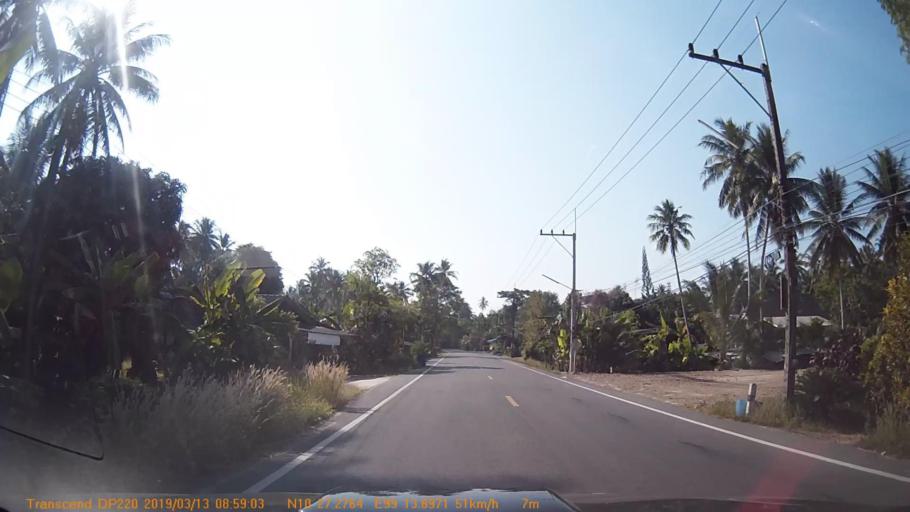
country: TH
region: Chumphon
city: Chumphon
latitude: 10.4544
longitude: 99.2317
